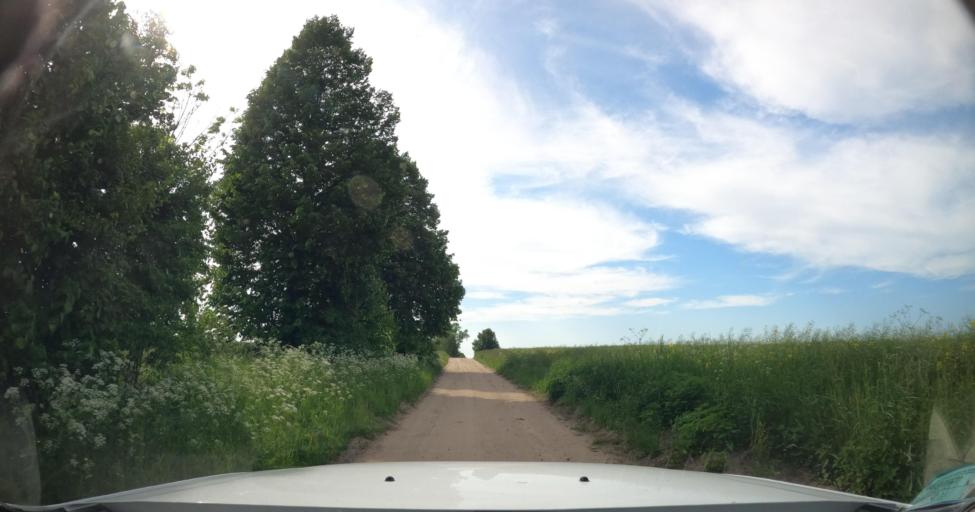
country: PL
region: Warmian-Masurian Voivodeship
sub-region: Powiat ostrodzki
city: Milakowo
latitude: 54.0160
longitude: 20.0098
